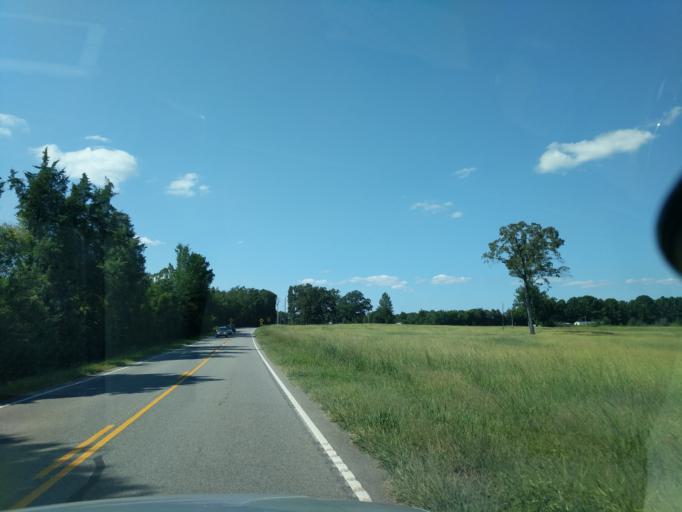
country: US
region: South Carolina
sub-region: Lexington County
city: Leesville
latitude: 34.0589
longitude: -81.5589
